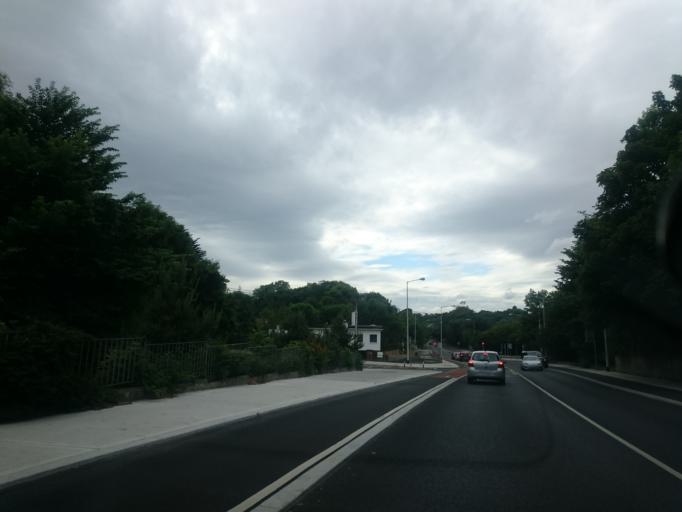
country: IE
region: Leinster
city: Rathgar
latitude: 53.3030
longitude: -6.2694
